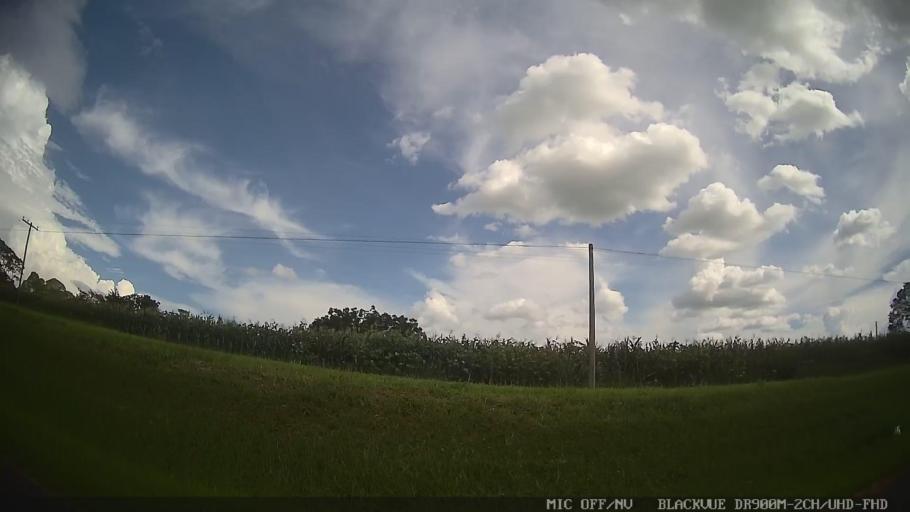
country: BR
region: Sao Paulo
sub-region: Laranjal Paulista
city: Laranjal Paulista
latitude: -23.0456
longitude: -47.9177
